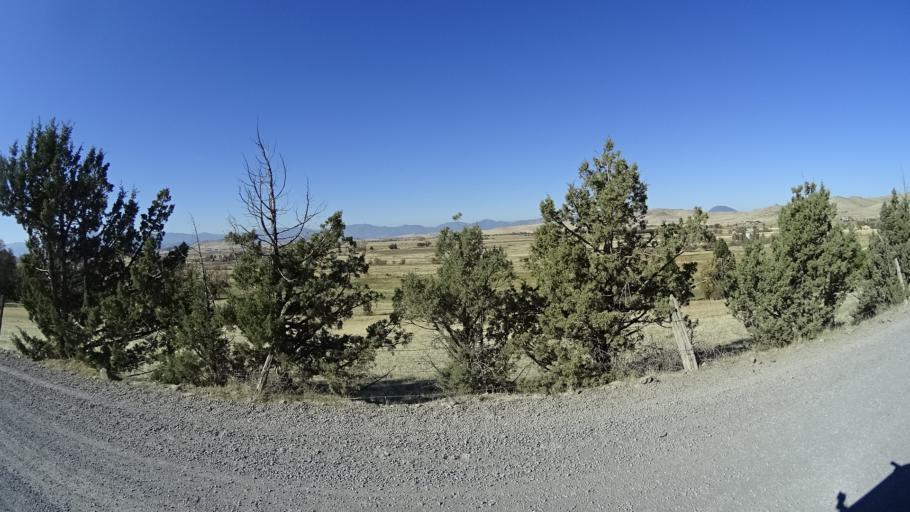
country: US
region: California
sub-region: Siskiyou County
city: Montague
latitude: 41.7133
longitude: -122.3760
